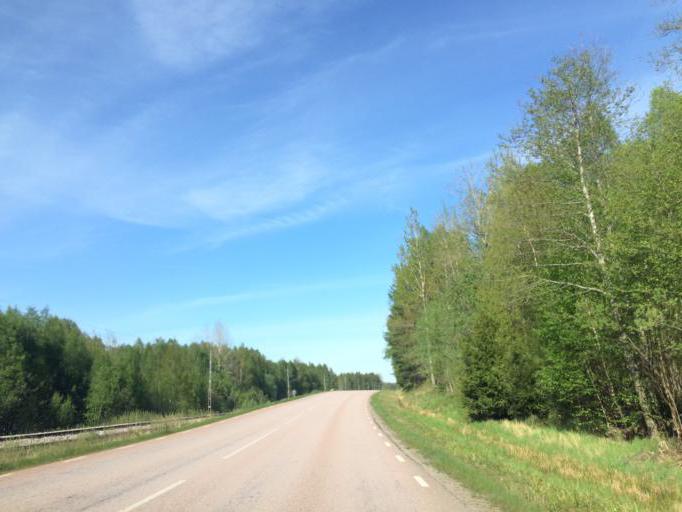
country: SE
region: Soedermanland
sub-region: Eskilstuna Kommun
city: Kvicksund
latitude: 59.4164
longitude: 16.2798
